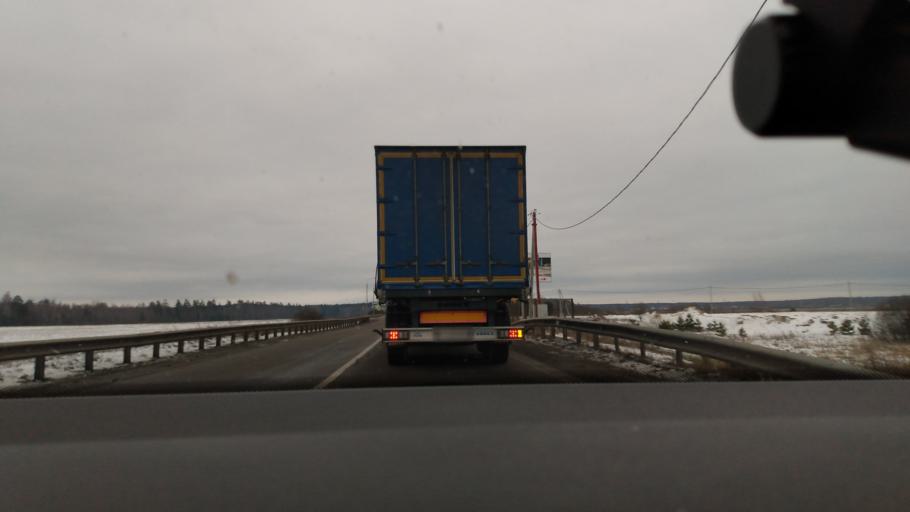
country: RU
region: Moskovskaya
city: Yegor'yevsk
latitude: 55.4406
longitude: 39.0194
